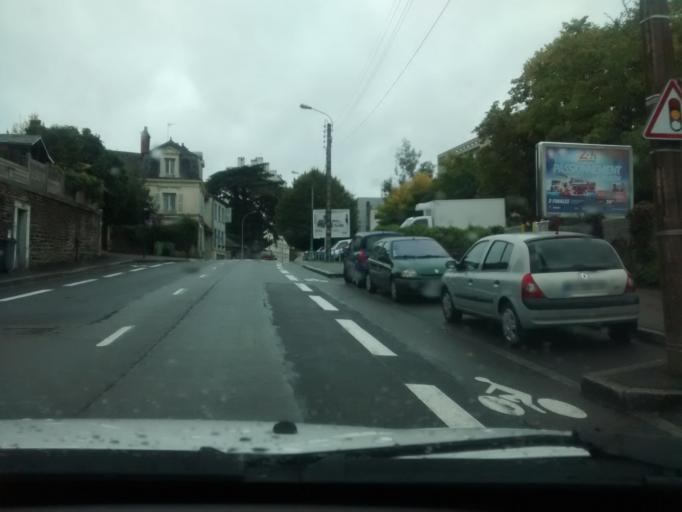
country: FR
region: Brittany
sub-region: Departement d'Ille-et-Vilaine
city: Rennes
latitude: 48.1236
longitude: -1.6685
